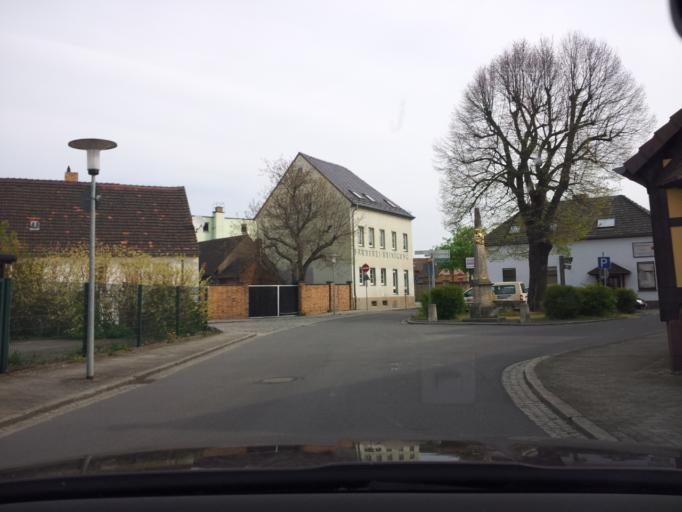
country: DE
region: Brandenburg
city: Lubbenau
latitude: 51.8670
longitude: 13.9555
